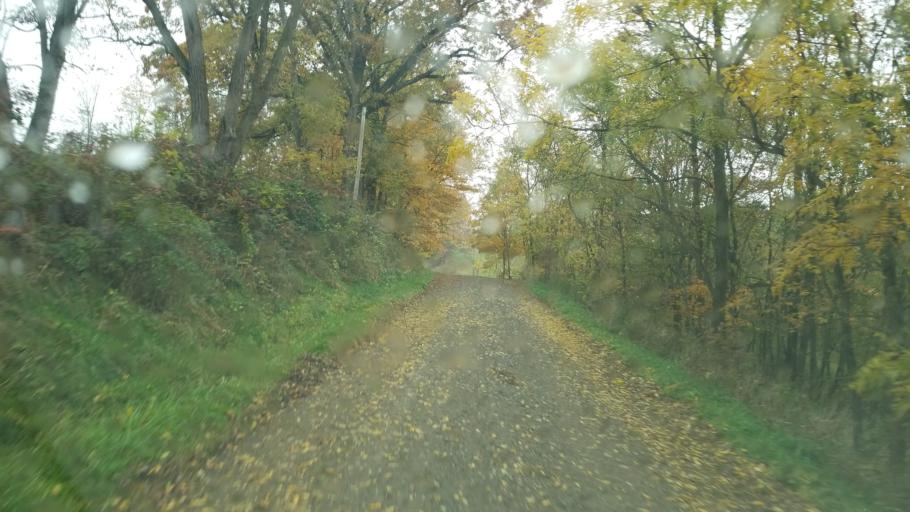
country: US
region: Ohio
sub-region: Holmes County
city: Millersburg
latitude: 40.4320
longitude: -81.8655
